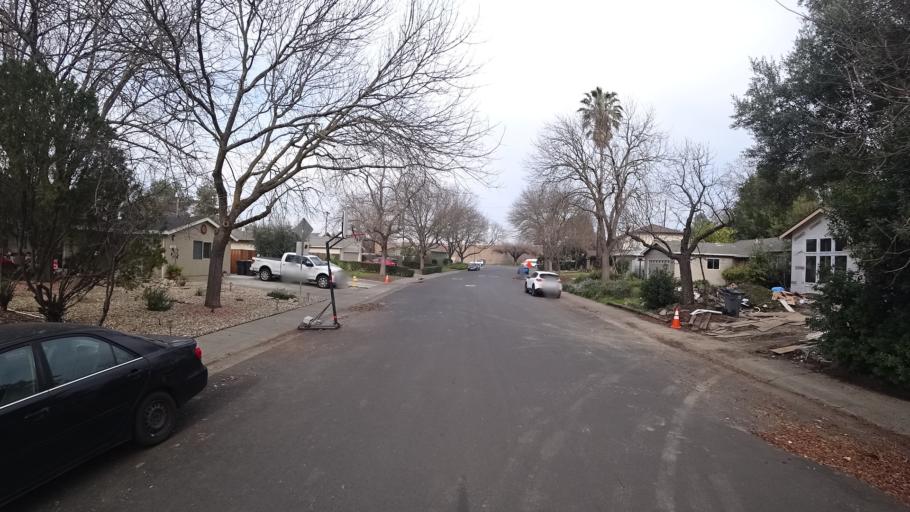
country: US
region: California
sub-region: Yolo County
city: Davis
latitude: 38.5596
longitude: -121.7316
